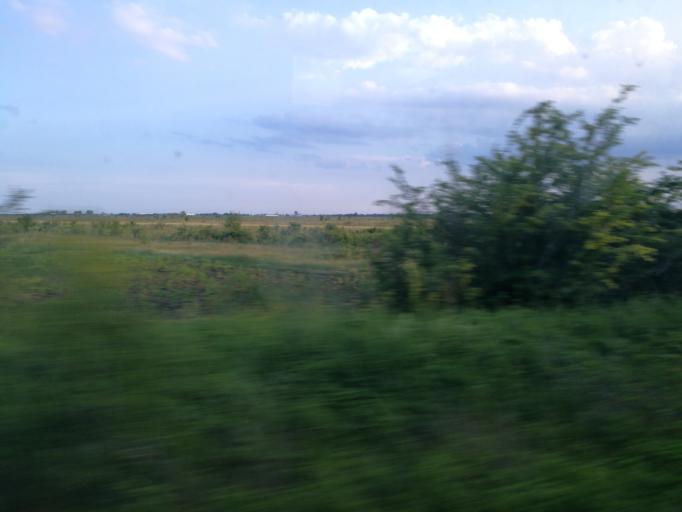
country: RO
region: Dambovita
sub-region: Comuna Titu
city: Salcuta
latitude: 44.6608
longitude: 25.6003
